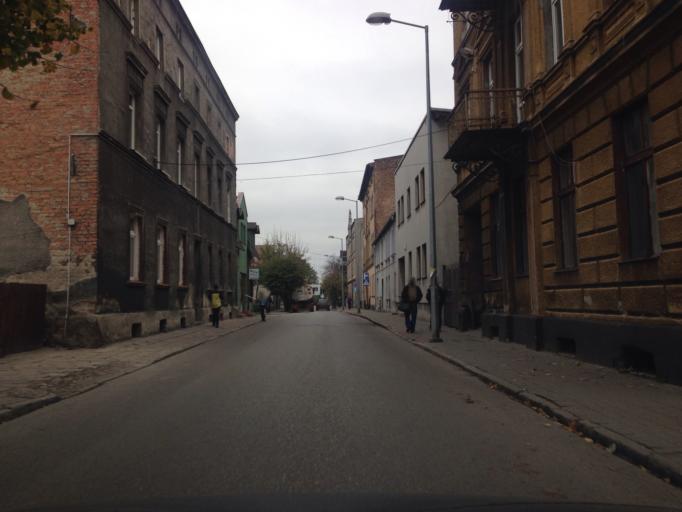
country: PL
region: Kujawsko-Pomorskie
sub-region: Powiat brodnicki
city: Brodnica
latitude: 53.2558
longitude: 19.4054
